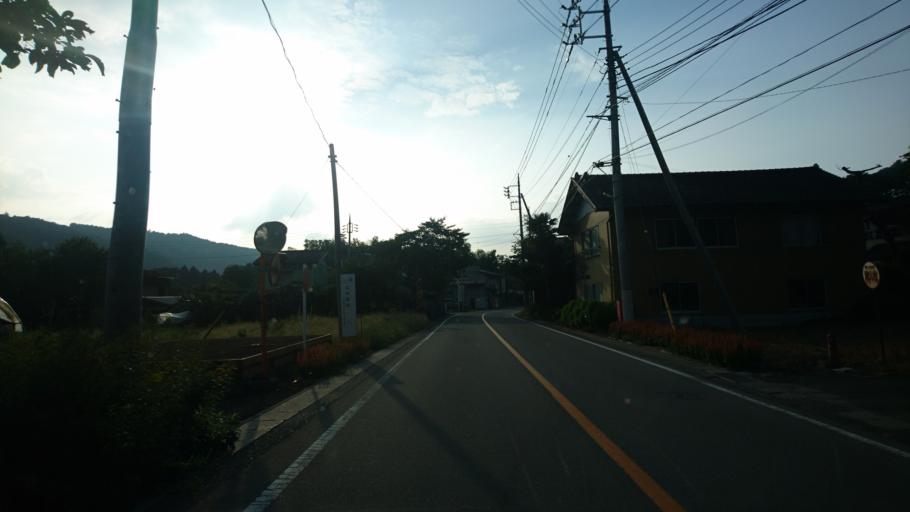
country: JP
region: Gunma
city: Numata
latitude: 36.6476
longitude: 139.1524
